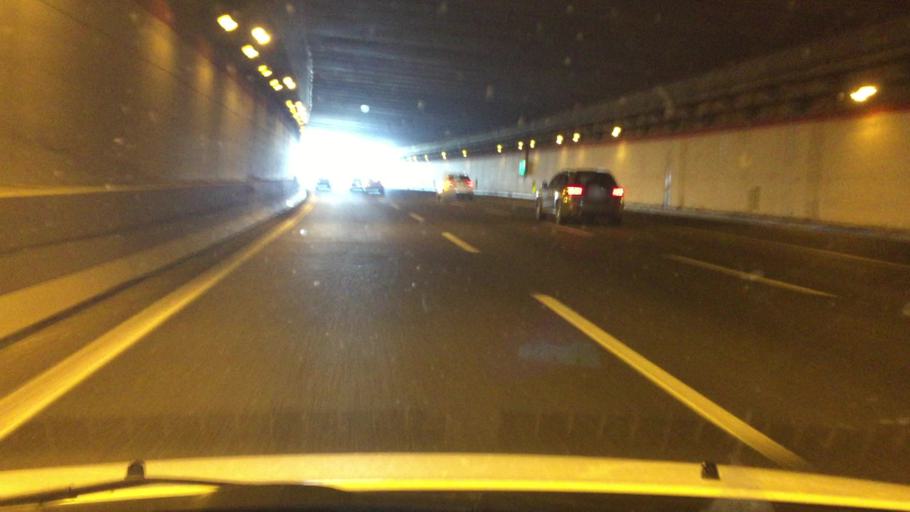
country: VA
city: Vatican City
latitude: 41.9814
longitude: 12.4523
